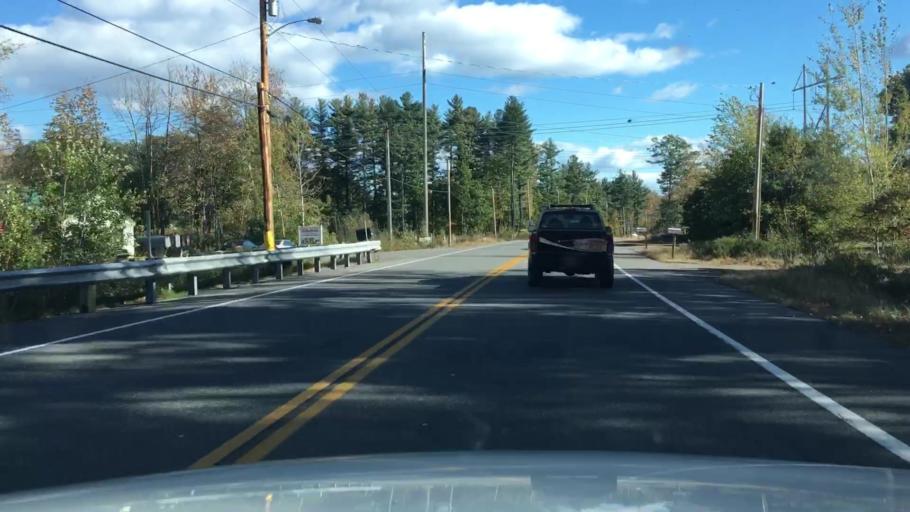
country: US
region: Maine
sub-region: York County
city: Wells Beach Station
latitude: 43.3540
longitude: -70.6513
